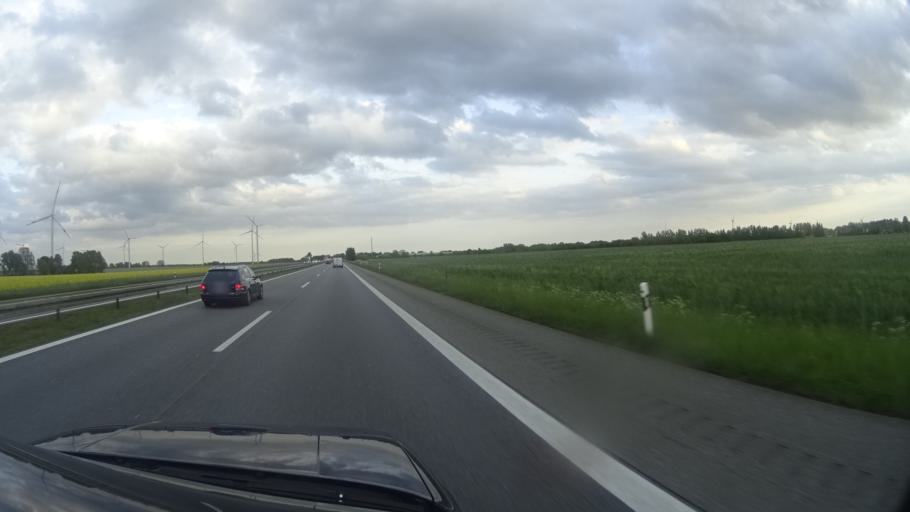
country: DE
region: Brandenburg
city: Dabergotz
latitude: 52.9222
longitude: 12.7150
